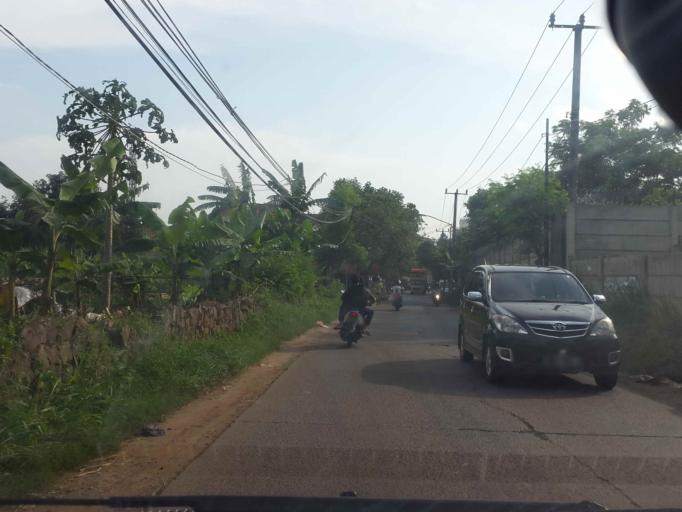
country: ID
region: West Java
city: Ciputat
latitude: -6.2692
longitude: 106.6710
